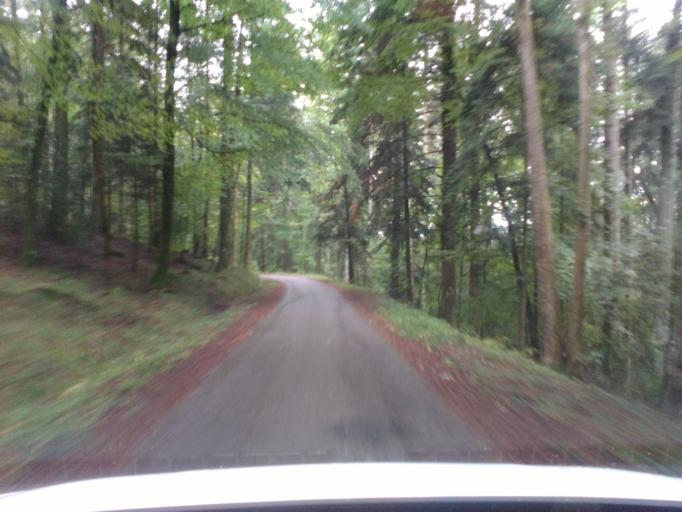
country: FR
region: Lorraine
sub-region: Departement des Vosges
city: Sainte-Marguerite
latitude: 48.3216
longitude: 7.0055
